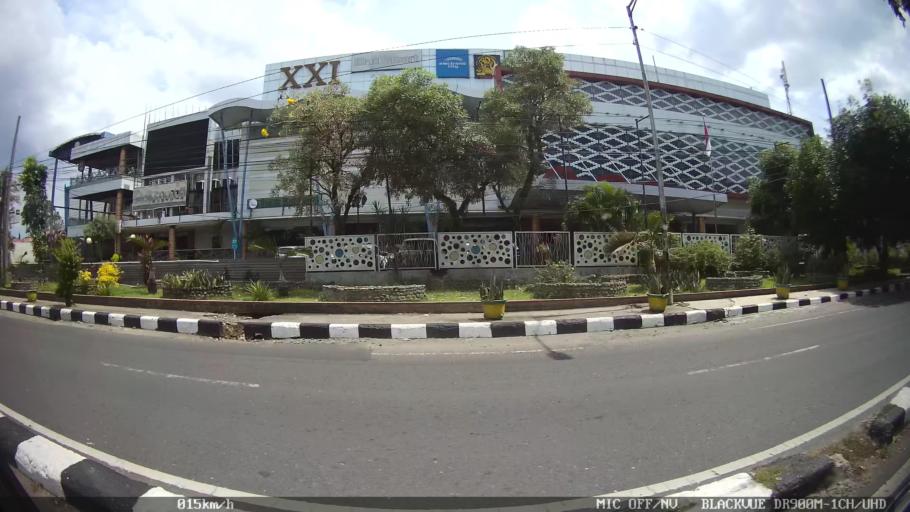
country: ID
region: North Sumatra
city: Medan
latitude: 3.5712
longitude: 98.6655
